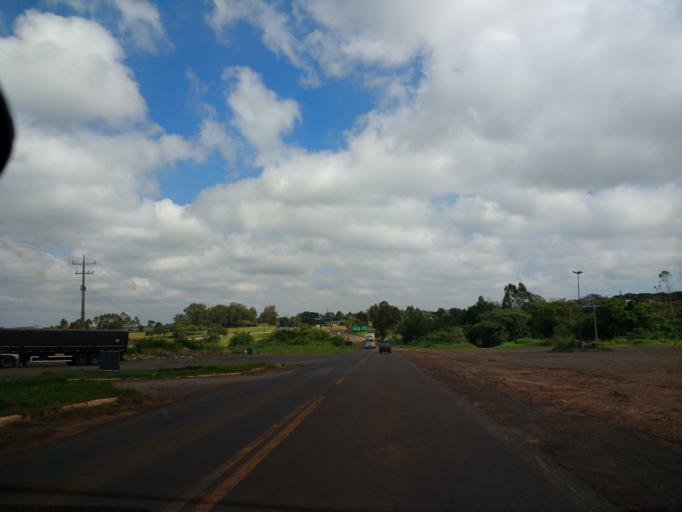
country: BR
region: Parana
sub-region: Cruzeiro Do Oeste
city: Cruzeiro do Oeste
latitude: -23.7928
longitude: -53.0426
